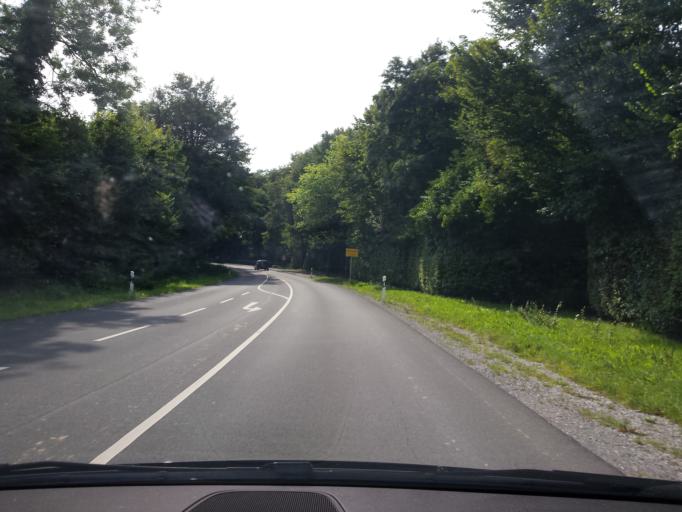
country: DE
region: North Rhine-Westphalia
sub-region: Regierungsbezirk Munster
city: Wadersloh
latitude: 51.6565
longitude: 8.2480
